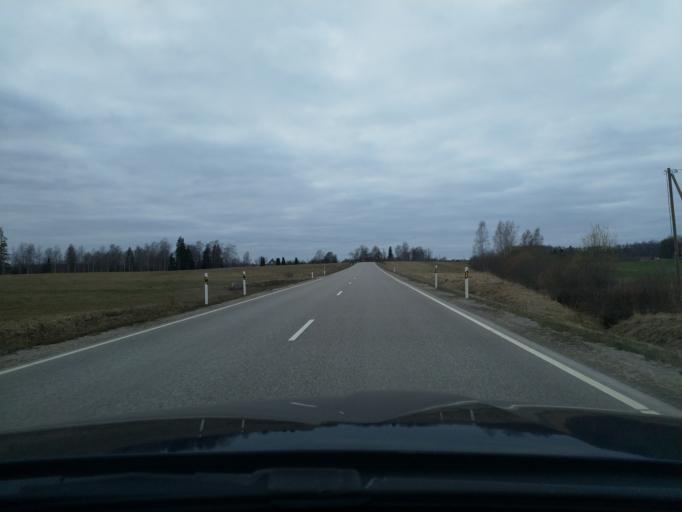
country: LV
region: Talsu Rajons
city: Sabile
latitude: 56.9296
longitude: 22.5397
